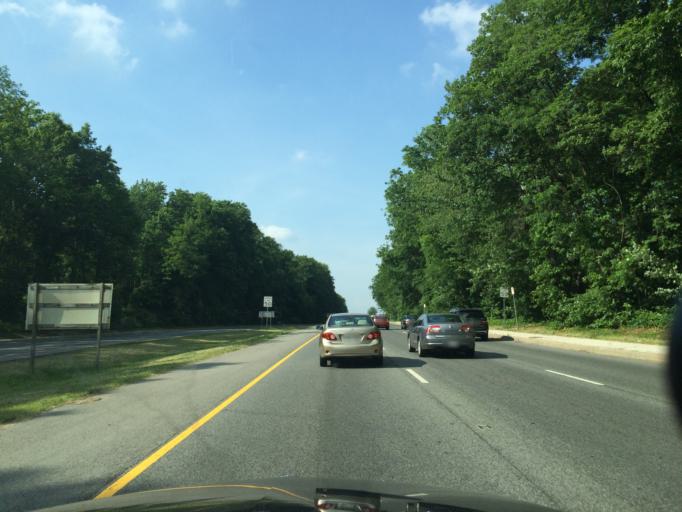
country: US
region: Maryland
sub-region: Montgomery County
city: Rossmoor
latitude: 39.0948
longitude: -77.0791
